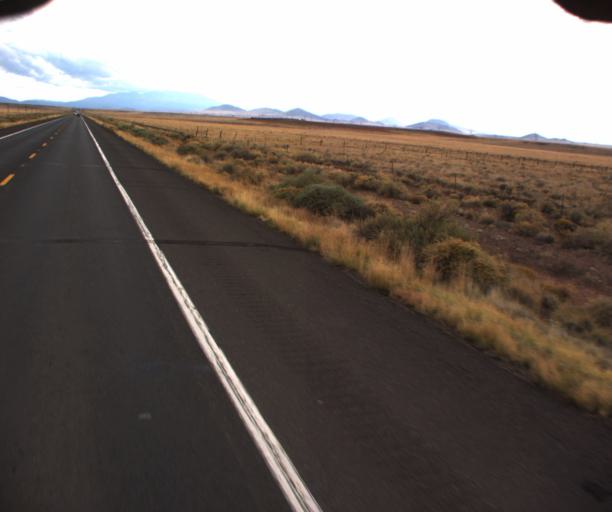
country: US
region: Arizona
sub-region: Coconino County
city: Flagstaff
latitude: 35.6827
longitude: -111.5068
